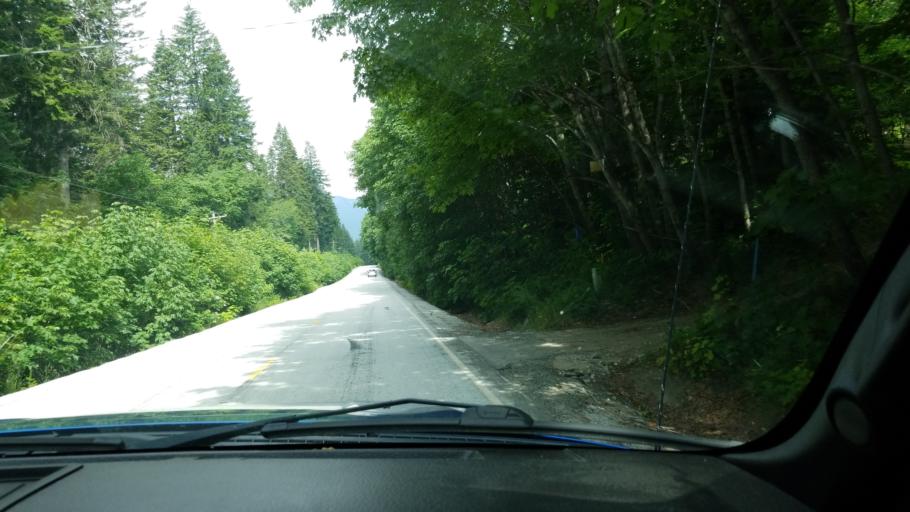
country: US
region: Washington
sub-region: Chelan County
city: Leavenworth
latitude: 47.8406
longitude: -120.8056
